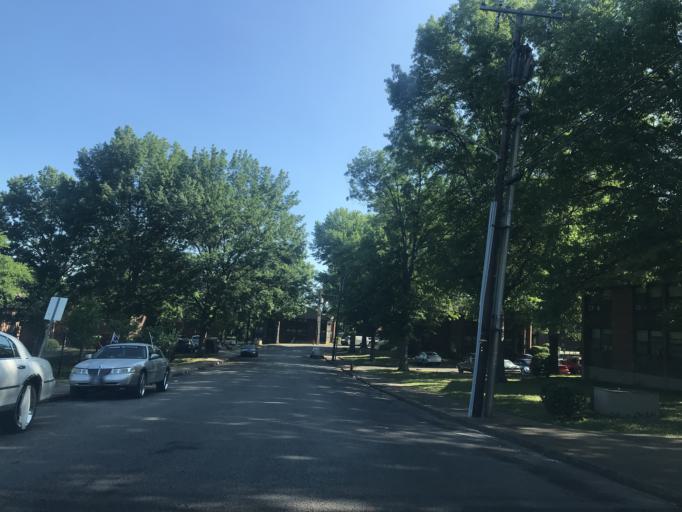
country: US
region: Tennessee
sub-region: Davidson County
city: Nashville
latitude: 36.1895
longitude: -86.8180
